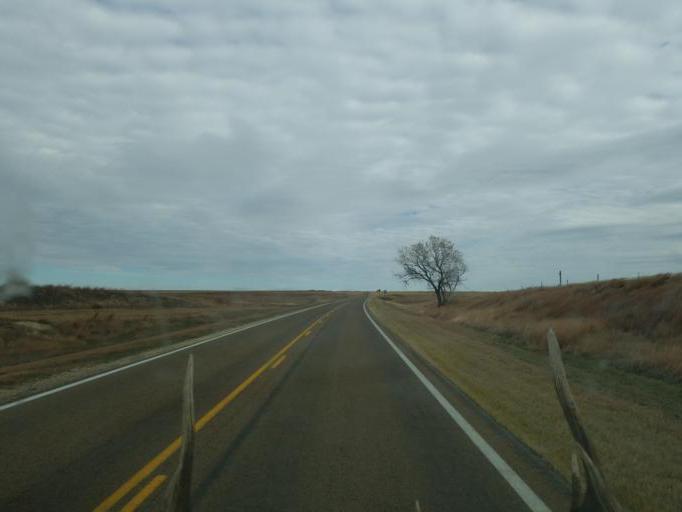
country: US
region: Kansas
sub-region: Wallace County
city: Sharon Springs
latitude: 39.0219
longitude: -101.3373
